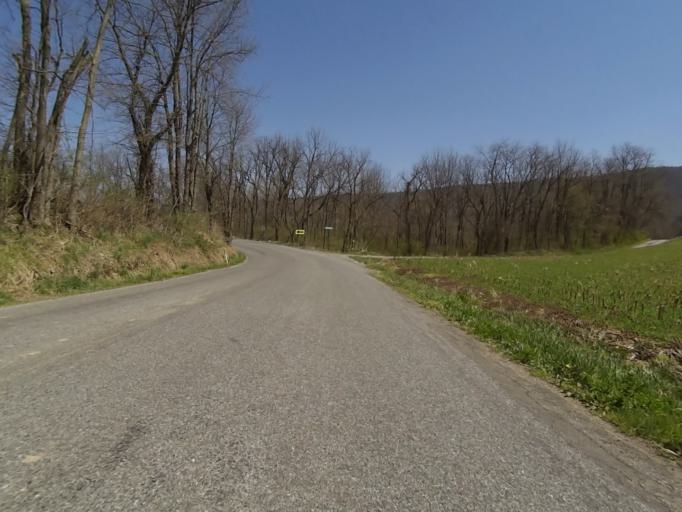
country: US
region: Pennsylvania
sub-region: Blair County
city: Williamsburg
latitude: 40.4946
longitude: -78.1781
